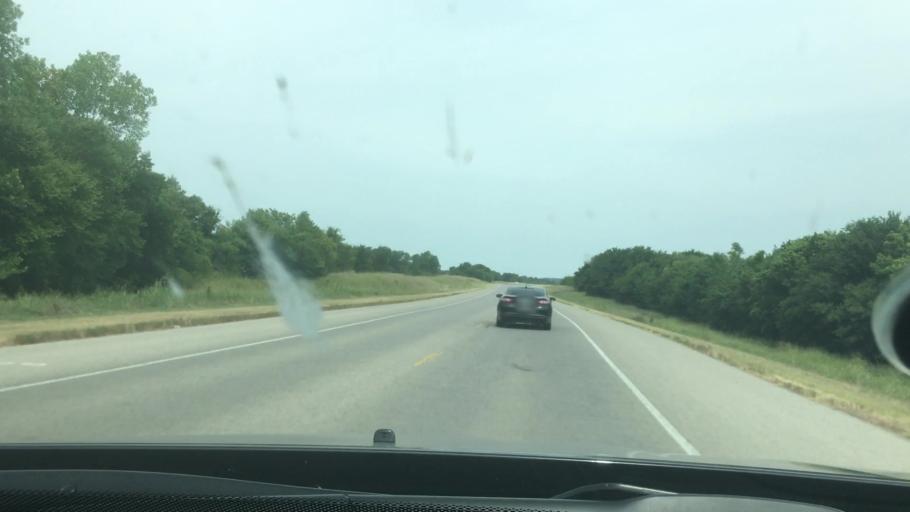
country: US
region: Oklahoma
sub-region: Pontotoc County
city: Ada
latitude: 34.7027
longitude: -96.6047
